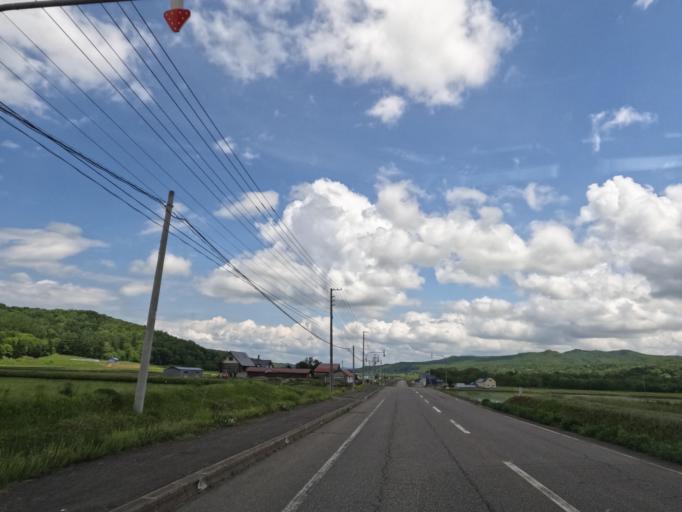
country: JP
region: Hokkaido
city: Takikawa
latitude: 43.5893
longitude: 141.7607
